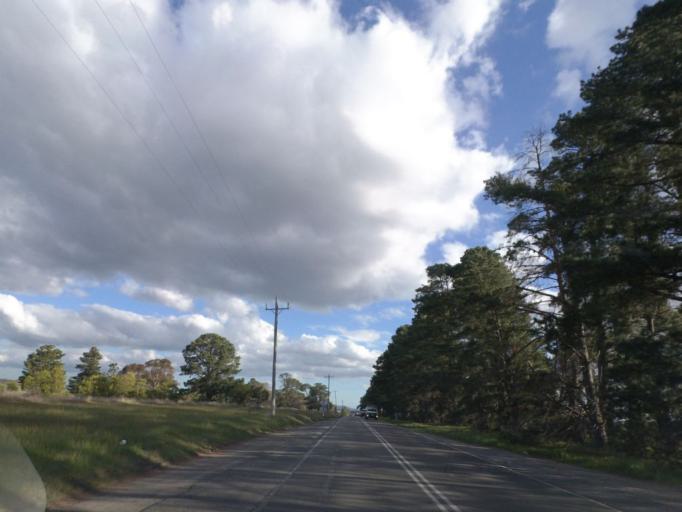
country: AU
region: Victoria
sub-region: Yarra Ranges
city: Yarra Glen
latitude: -37.6915
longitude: 145.3741
